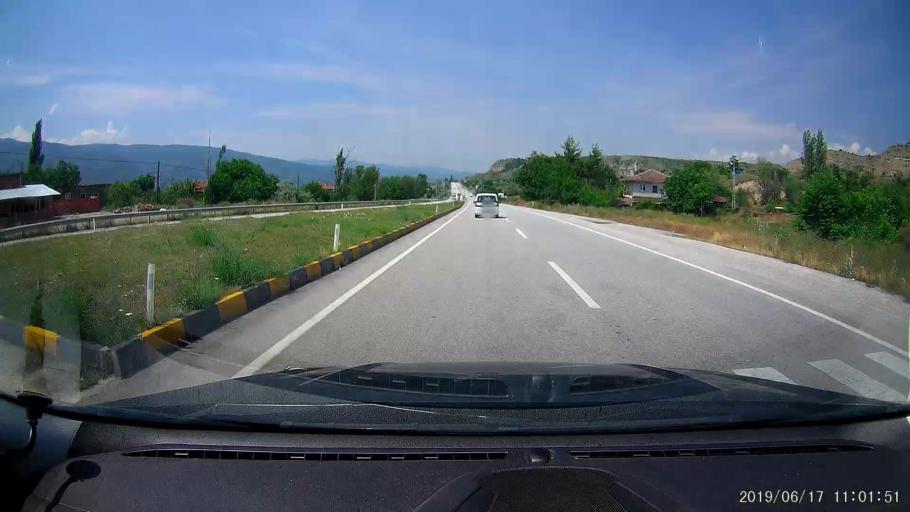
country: TR
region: Kastamonu
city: Tosya
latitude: 41.0237
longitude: 34.1471
